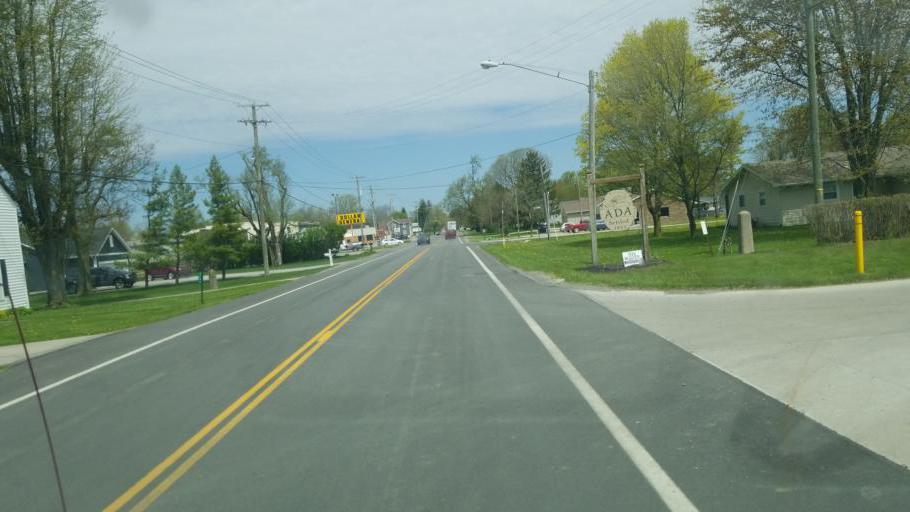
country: US
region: Ohio
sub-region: Hardin County
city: Ada
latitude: 40.7583
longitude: -83.8231
